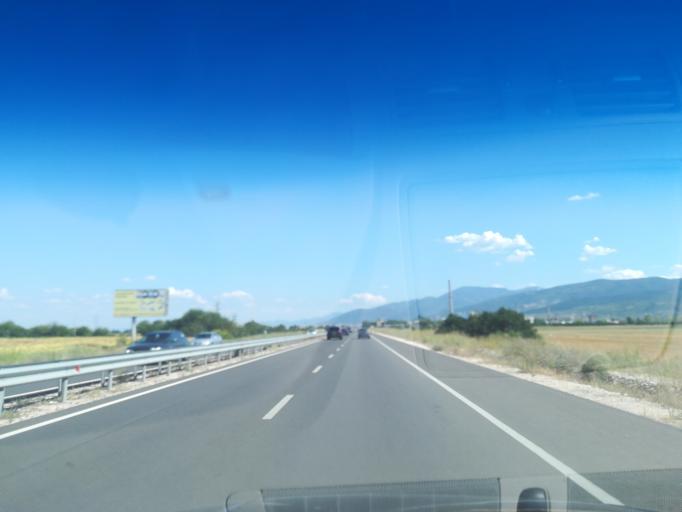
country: BG
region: Plovdiv
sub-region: Obshtina Asenovgrad
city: Asenovgrad
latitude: 42.0758
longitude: 24.8057
